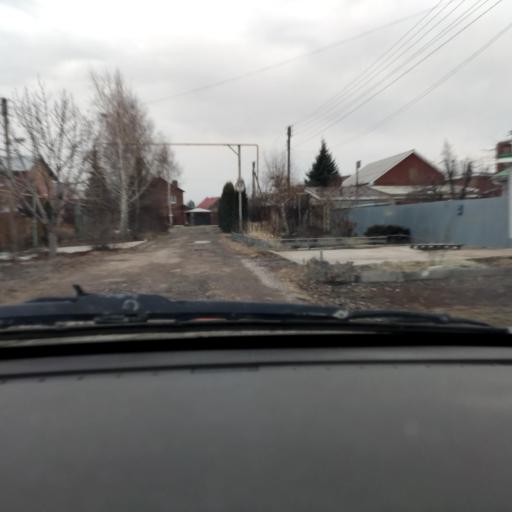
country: RU
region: Samara
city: Podstepki
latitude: 53.5173
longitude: 49.1864
